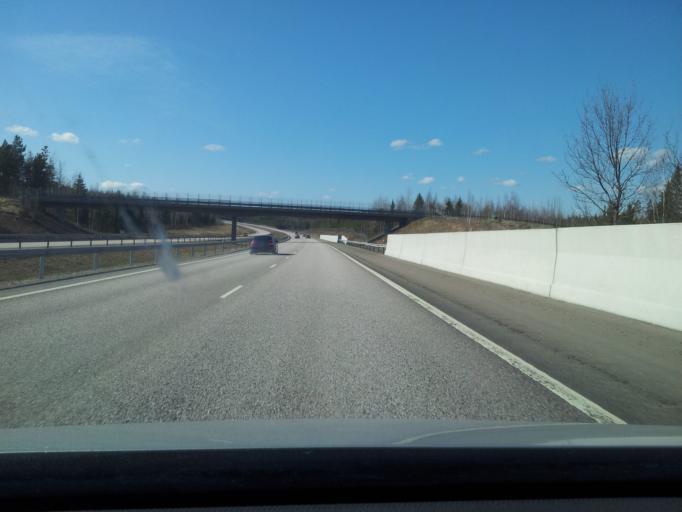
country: FI
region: Uusimaa
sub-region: Loviisa
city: Perna
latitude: 60.4725
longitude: 26.1207
